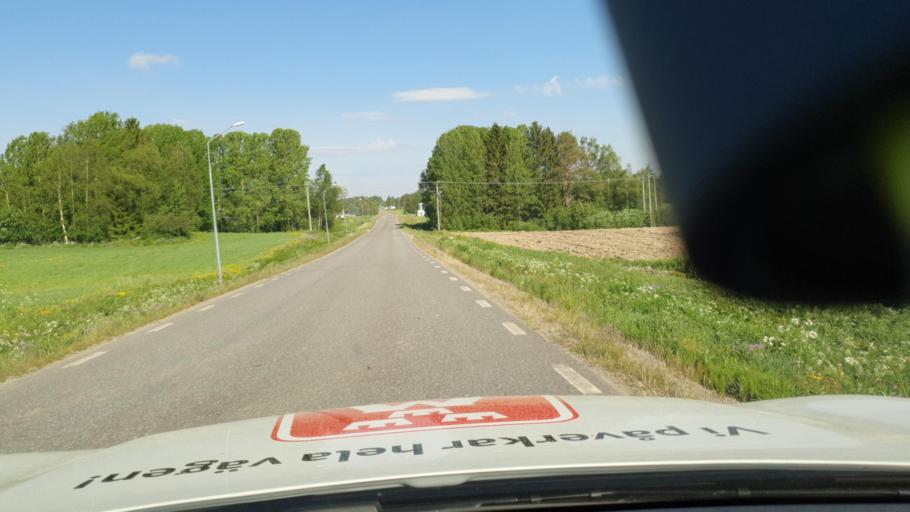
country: SE
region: Vaesterbotten
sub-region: Robertsfors Kommun
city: Robertsfors
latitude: 64.3660
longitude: 20.9174
